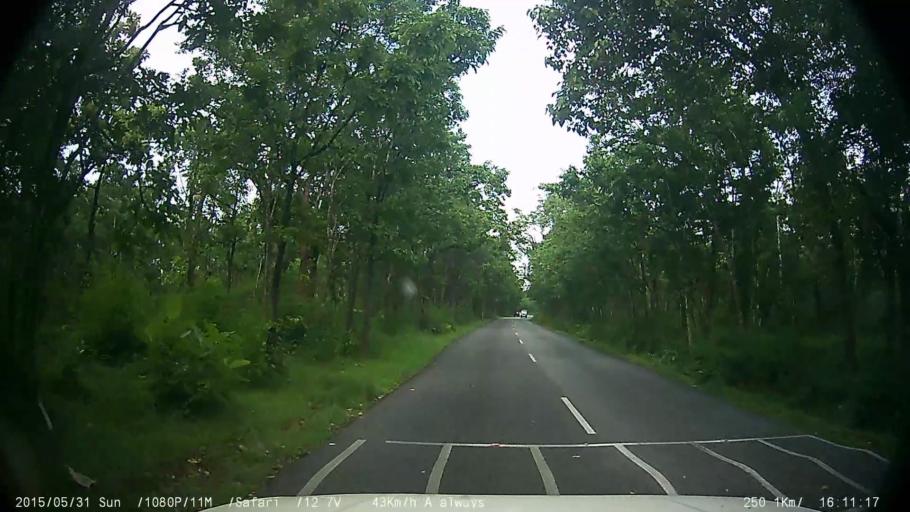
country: IN
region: Tamil Nadu
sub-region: Nilgiri
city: Masinigudi
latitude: 11.7289
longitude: 76.4443
